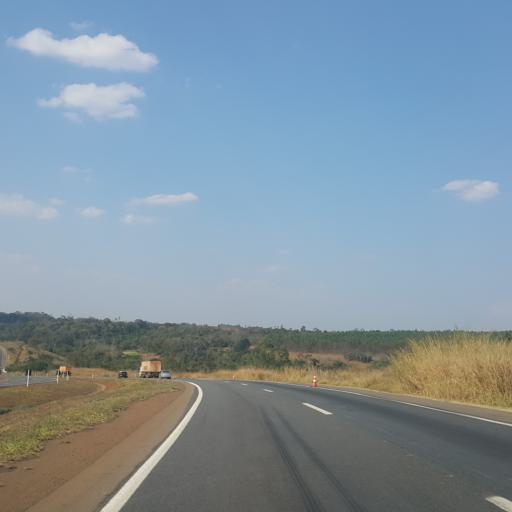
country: BR
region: Goias
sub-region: Abadiania
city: Abadiania
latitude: -16.2765
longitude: -48.7792
